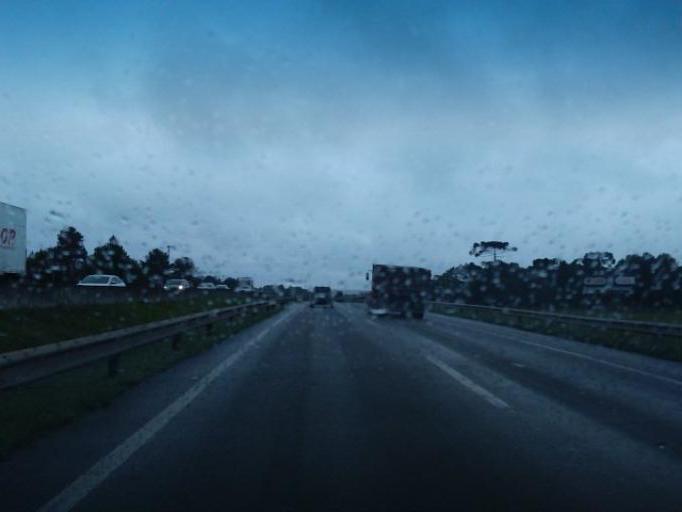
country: BR
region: Parana
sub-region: Sao Jose Dos Pinhais
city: Sao Jose dos Pinhais
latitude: -25.6666
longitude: -49.1531
